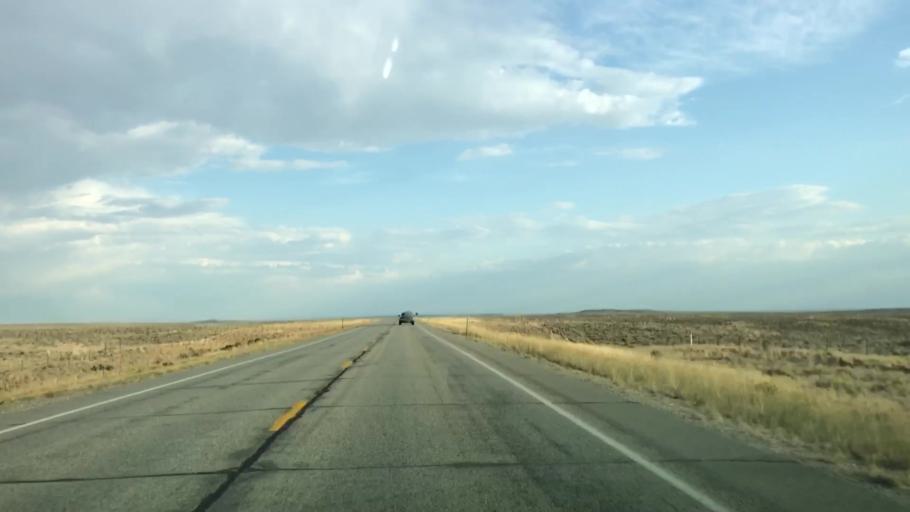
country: US
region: Wyoming
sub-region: Sublette County
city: Pinedale
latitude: 42.3964
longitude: -109.5438
